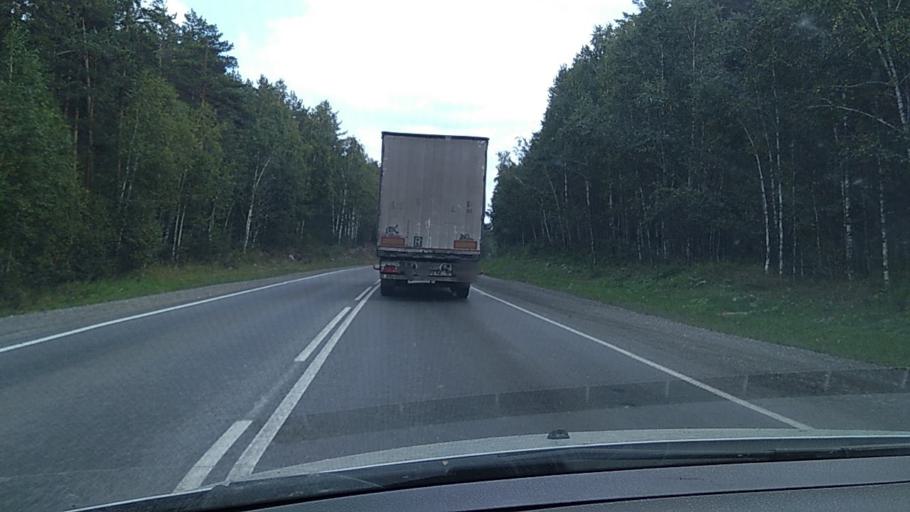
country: RU
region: Chelyabinsk
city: Miass
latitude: 54.9448
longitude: 60.1052
